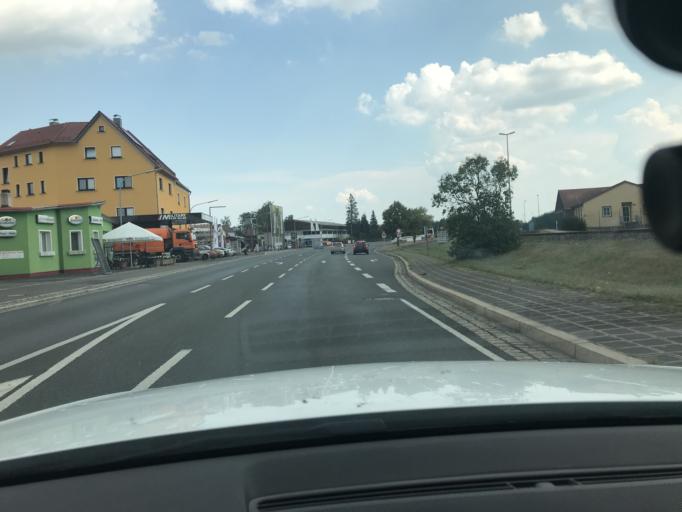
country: DE
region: Bavaria
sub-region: Upper Palatinate
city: Grafenwohr
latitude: 49.7168
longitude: 11.9145
